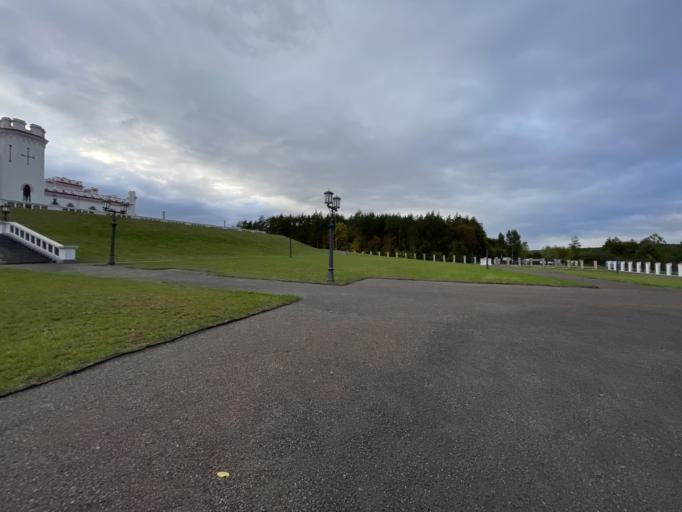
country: BY
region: Brest
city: Kosava
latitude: 52.7661
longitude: 25.1225
